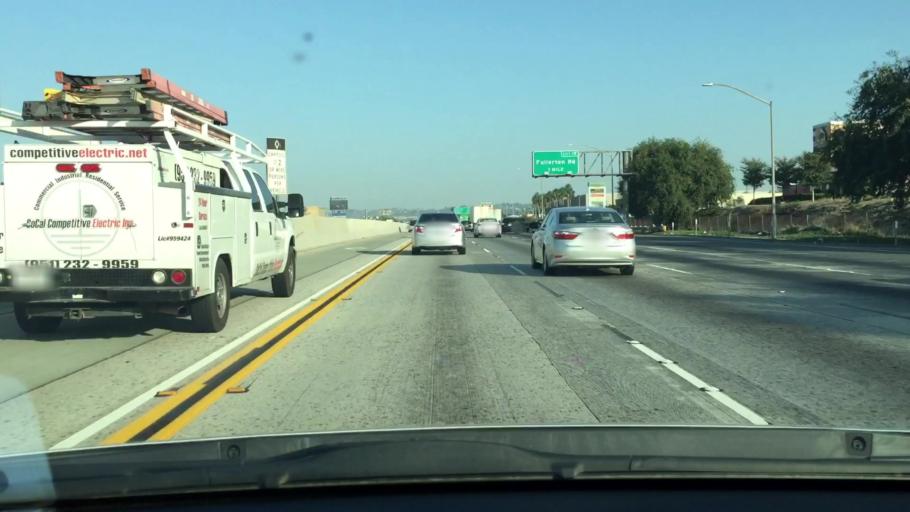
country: US
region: California
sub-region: Los Angeles County
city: South San Jose Hills
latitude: 33.9966
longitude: -117.9269
